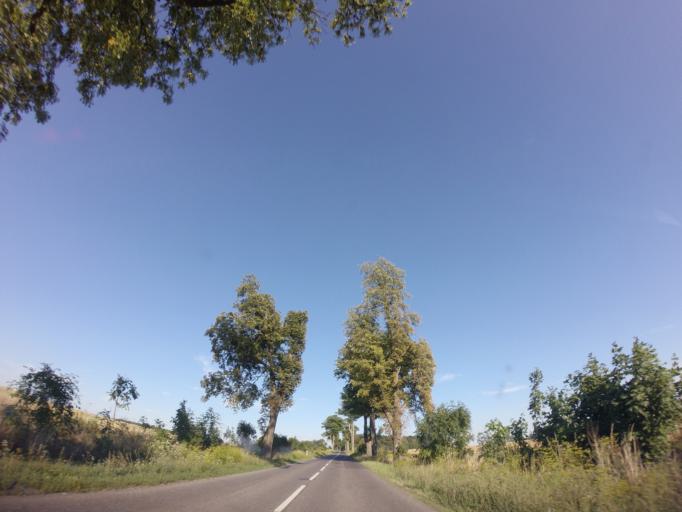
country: PL
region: Lubusz
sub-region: Powiat gorzowski
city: Santok
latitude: 52.7541
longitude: 15.3697
